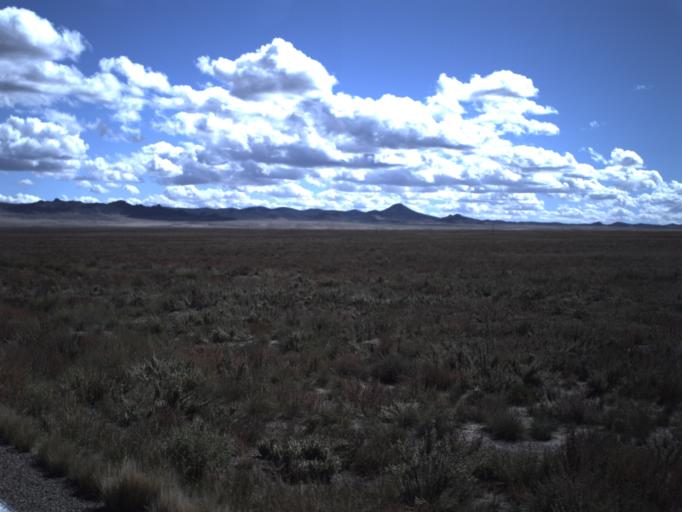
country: US
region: Utah
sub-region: Beaver County
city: Milford
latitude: 38.4706
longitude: -113.4073
